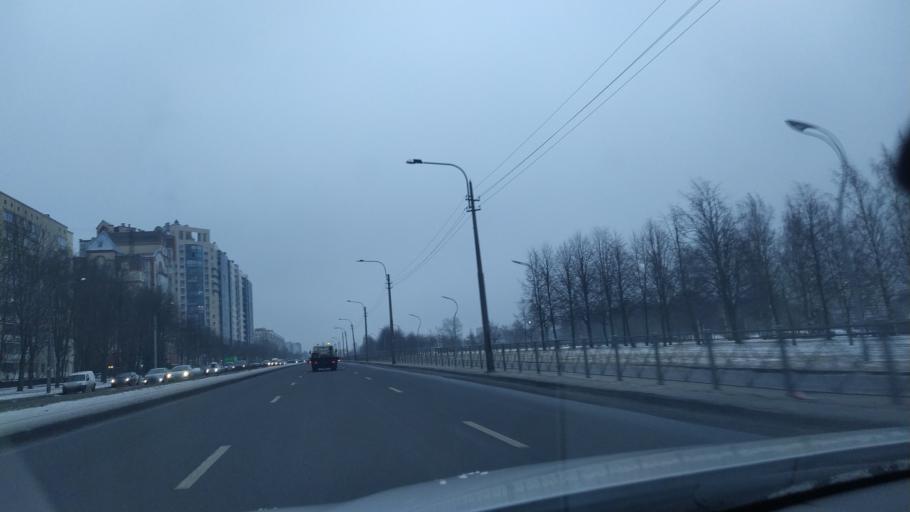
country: RU
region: St.-Petersburg
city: Grazhdanka
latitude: 60.0299
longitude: 30.3953
